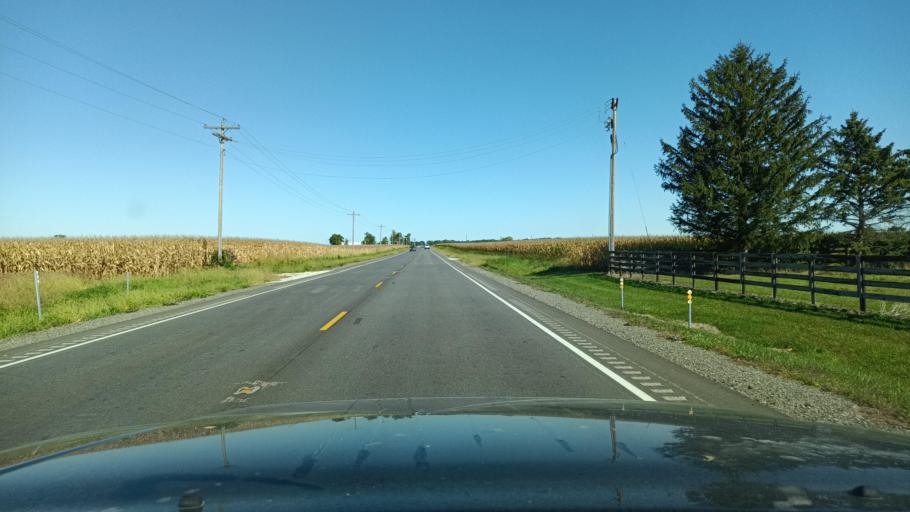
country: US
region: Illinois
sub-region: Champaign County
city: Philo
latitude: 39.9741
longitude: -88.1612
